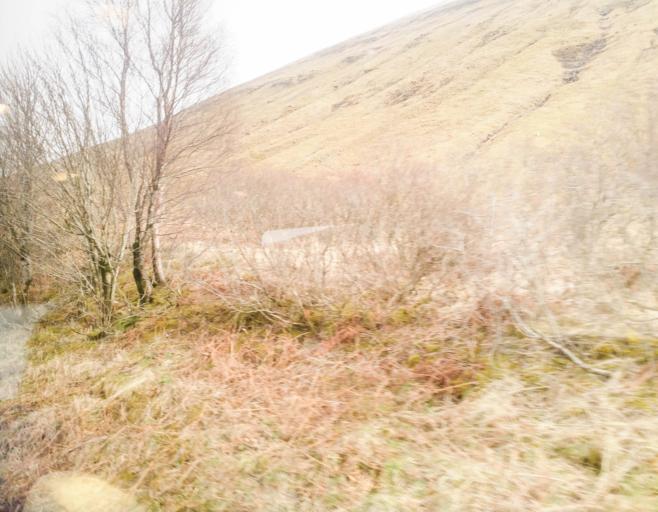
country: GB
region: Scotland
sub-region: Argyll and Bute
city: Garelochhead
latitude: 56.4646
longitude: -4.7153
